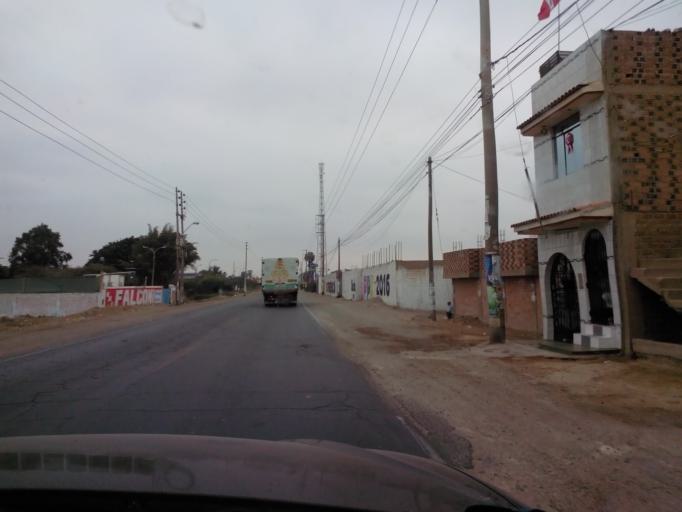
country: PE
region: Ica
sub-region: Provincia de Chincha
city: Chincha Baja
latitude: -13.4551
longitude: -76.1363
